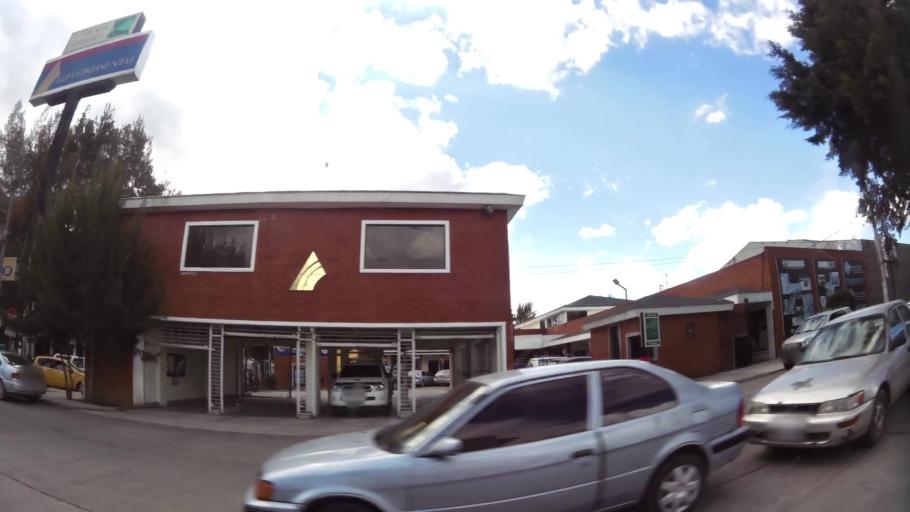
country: GT
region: Quetzaltenango
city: Quetzaltenango
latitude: 14.8452
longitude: -91.5260
